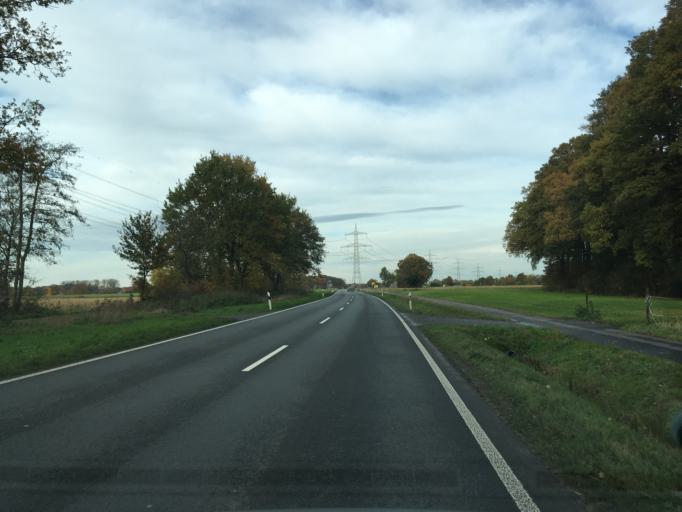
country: DE
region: North Rhine-Westphalia
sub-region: Regierungsbezirk Munster
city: Heiden
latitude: 51.8859
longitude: 6.9047
